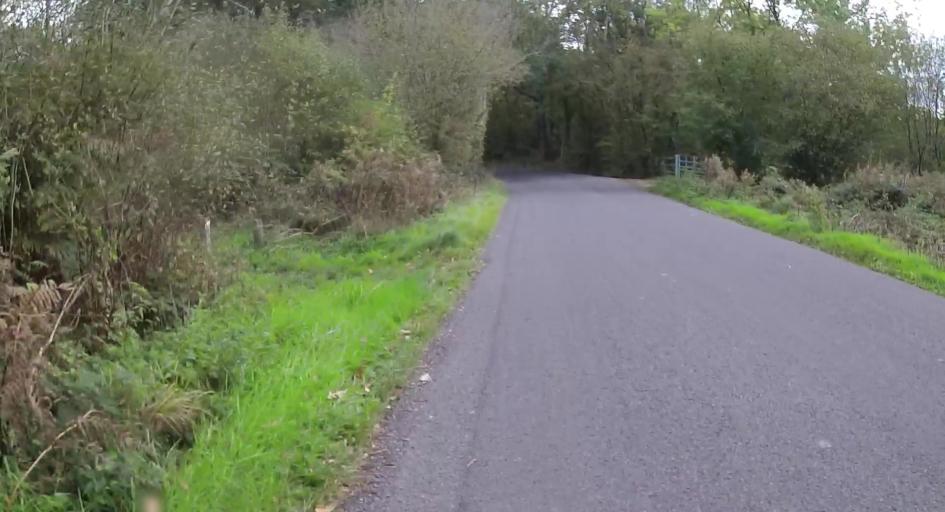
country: GB
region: England
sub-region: Hampshire
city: Odiham
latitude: 51.2687
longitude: -0.9149
